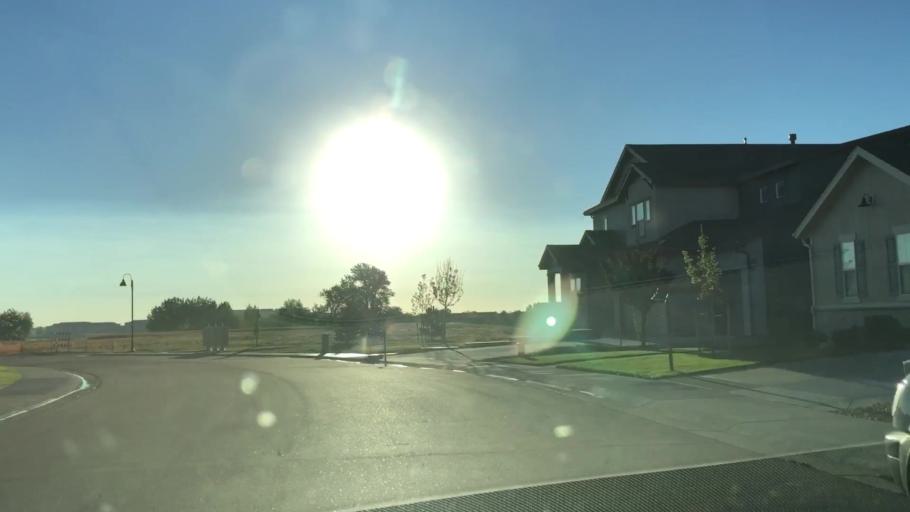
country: US
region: Colorado
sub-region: Larimer County
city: Loveland
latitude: 40.4148
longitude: -105.0153
